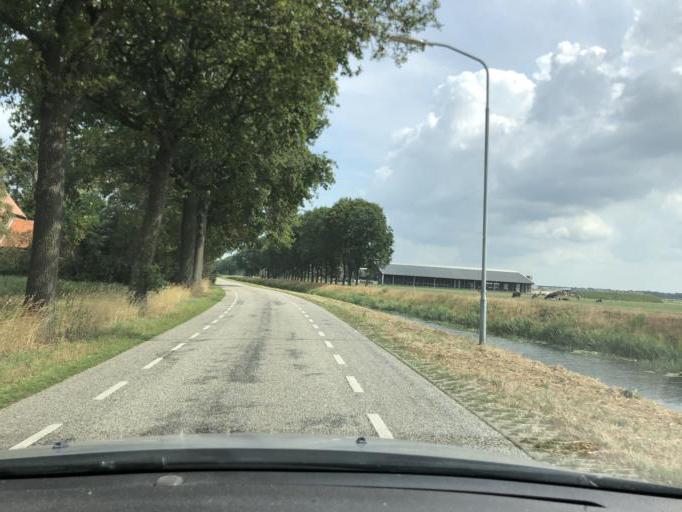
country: NL
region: Drenthe
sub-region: Gemeente Coevorden
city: Dalen
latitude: 52.7938
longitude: 6.6437
